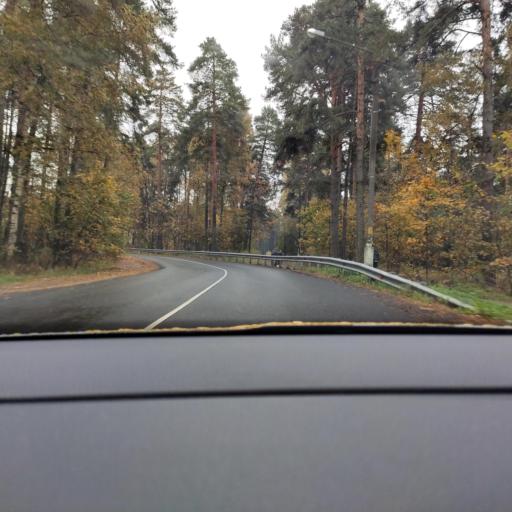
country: RU
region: Moskovskaya
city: Ivanteyevka
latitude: 55.9635
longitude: 37.9072
